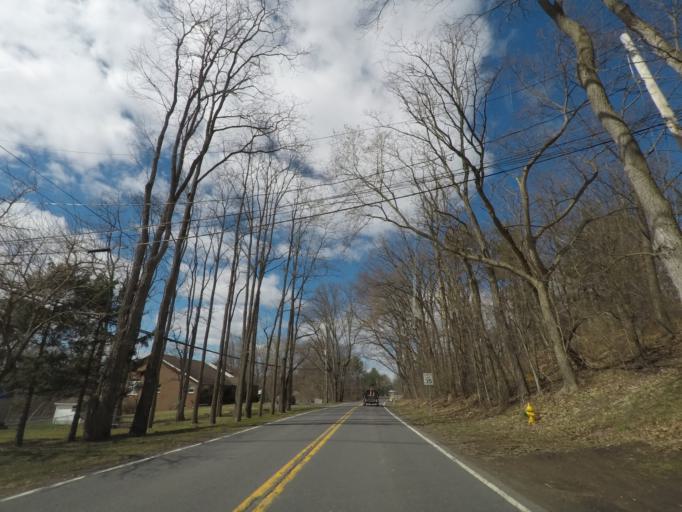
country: US
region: New York
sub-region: Albany County
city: Delmar
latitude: 42.5867
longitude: -73.8322
